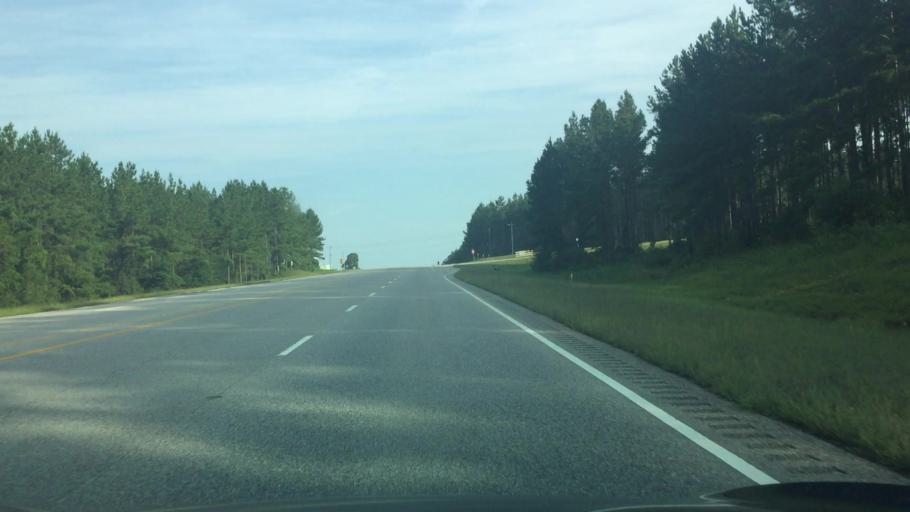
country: US
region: Alabama
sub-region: Butler County
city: Georgiana
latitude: 31.4809
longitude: -86.6762
